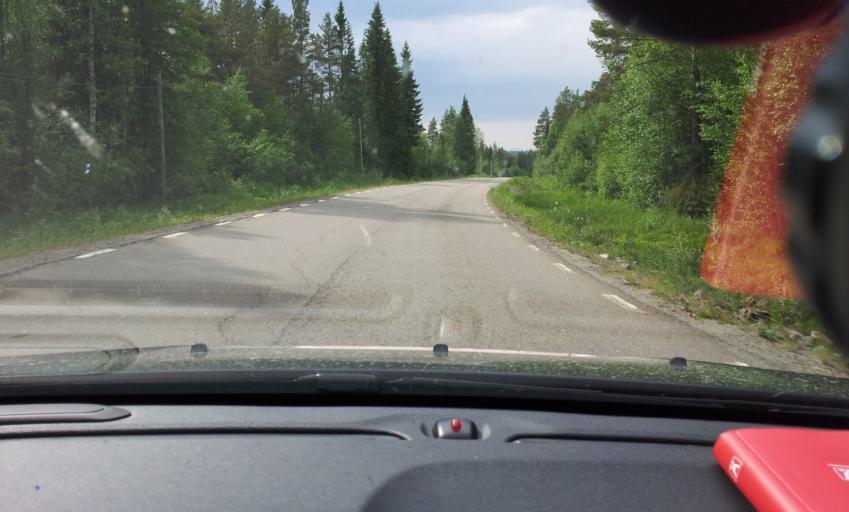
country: SE
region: Jaemtland
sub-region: Bergs Kommun
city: Hoverberg
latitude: 62.6620
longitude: 14.7716
